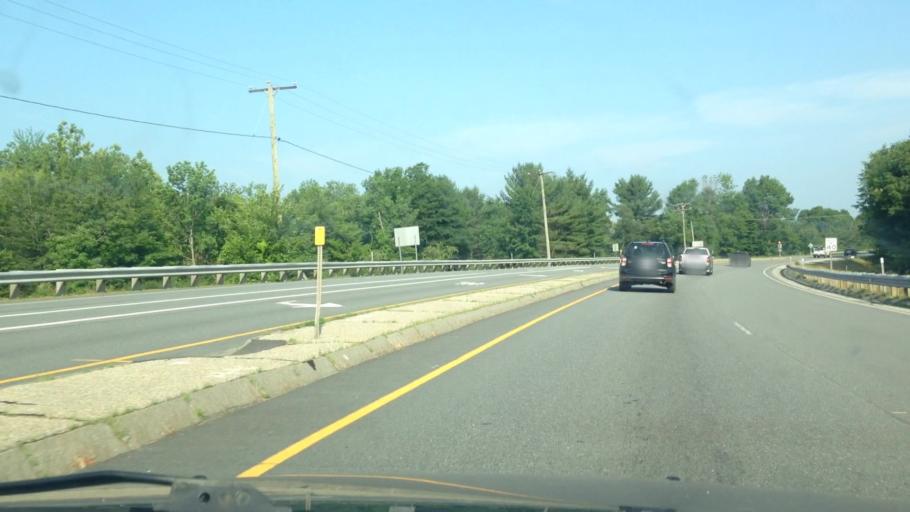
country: US
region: New Hampshire
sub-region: Cheshire County
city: Keene
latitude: 42.9158
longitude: -72.2638
